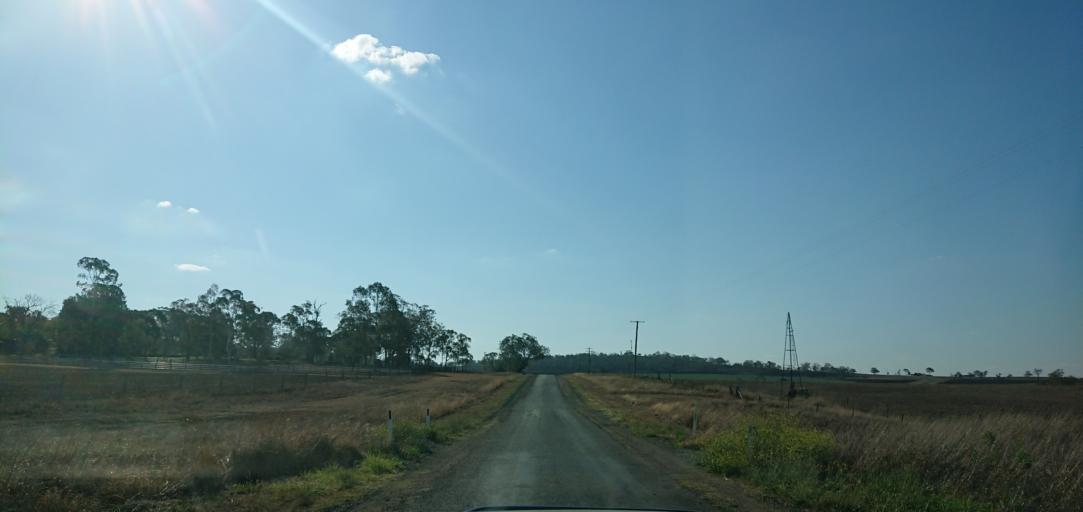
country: AU
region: Queensland
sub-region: Toowoomba
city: Westbrook
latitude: -27.7135
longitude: 151.7180
